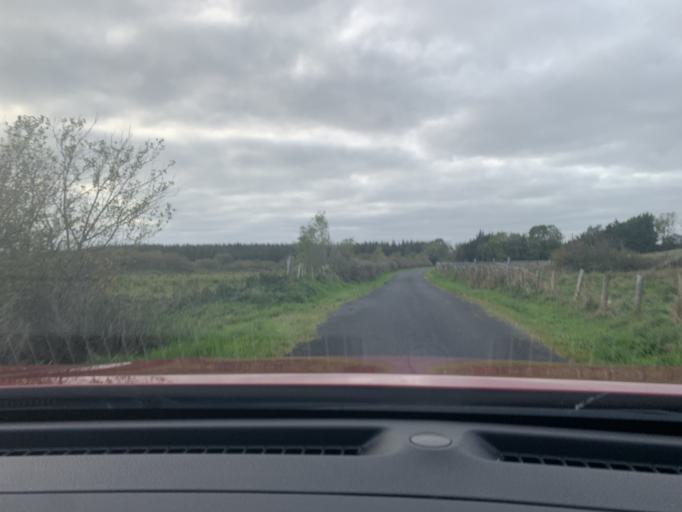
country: IE
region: Connaught
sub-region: Sligo
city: Tobercurry
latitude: 54.0185
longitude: -8.6291
